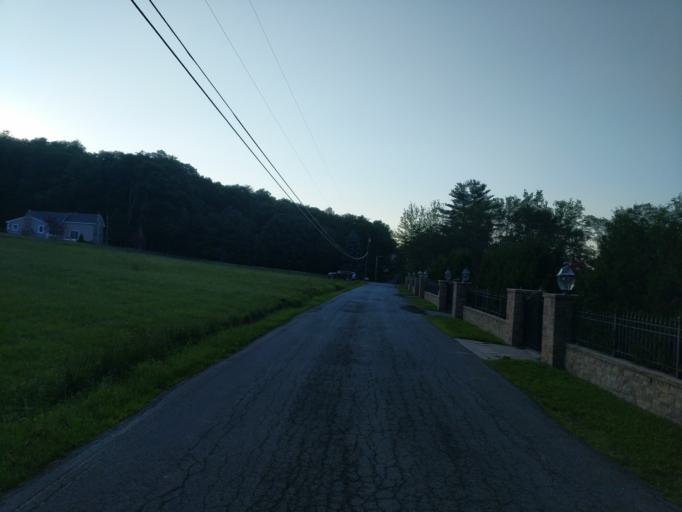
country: US
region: New York
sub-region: Sullivan County
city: Livingston Manor
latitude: 41.8864
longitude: -74.9793
